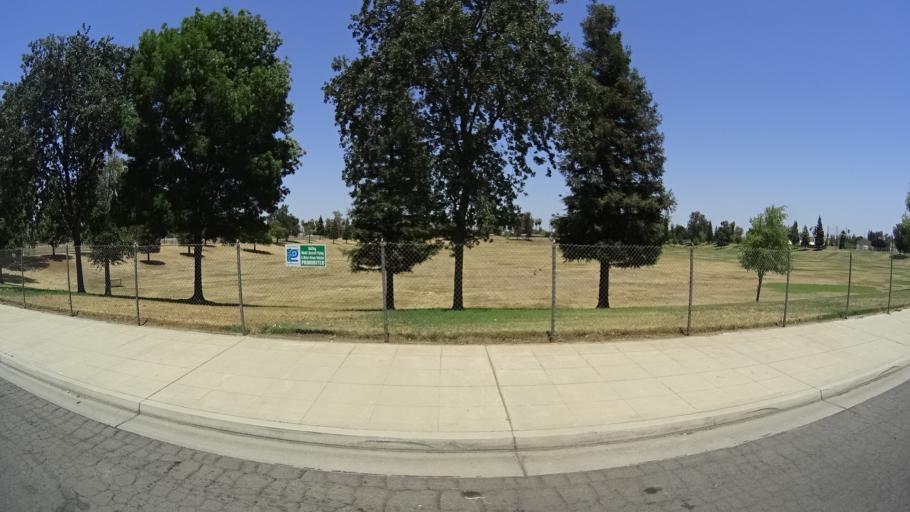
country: US
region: California
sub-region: Fresno County
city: West Park
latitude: 36.7249
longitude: -119.8256
